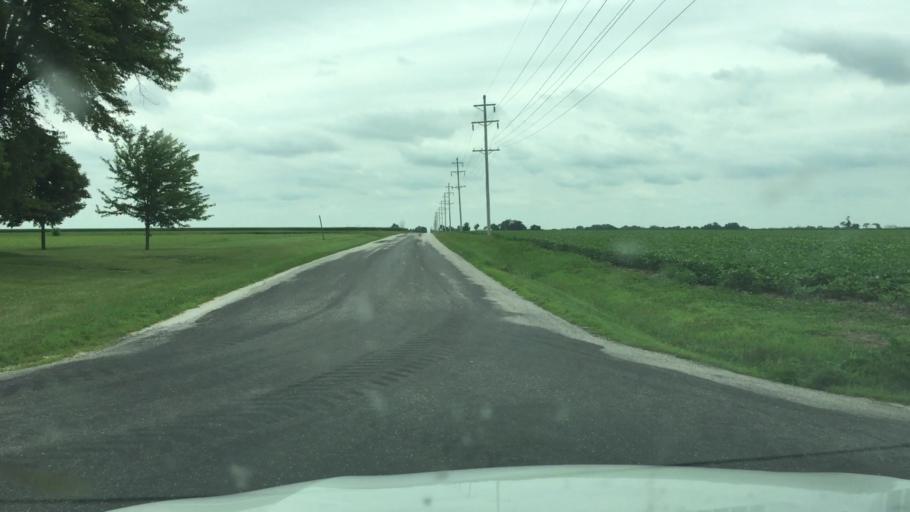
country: US
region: Illinois
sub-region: Hancock County
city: Carthage
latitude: 40.4008
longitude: -91.0825
